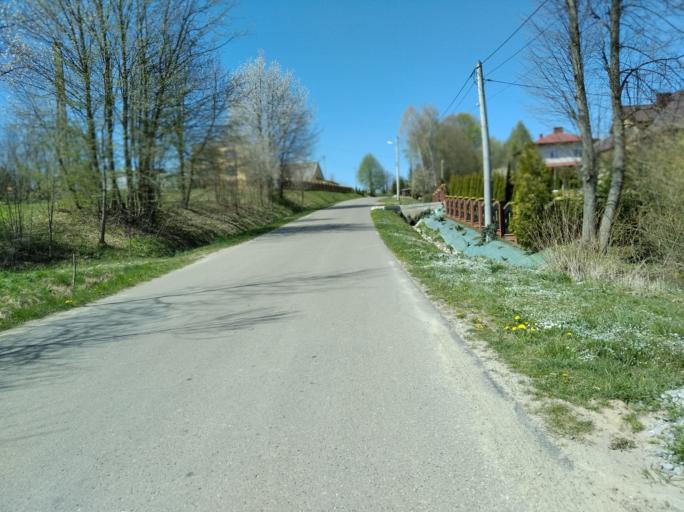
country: PL
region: Subcarpathian Voivodeship
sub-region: Powiat brzozowski
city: Jablonka
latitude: 49.7229
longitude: 22.1171
